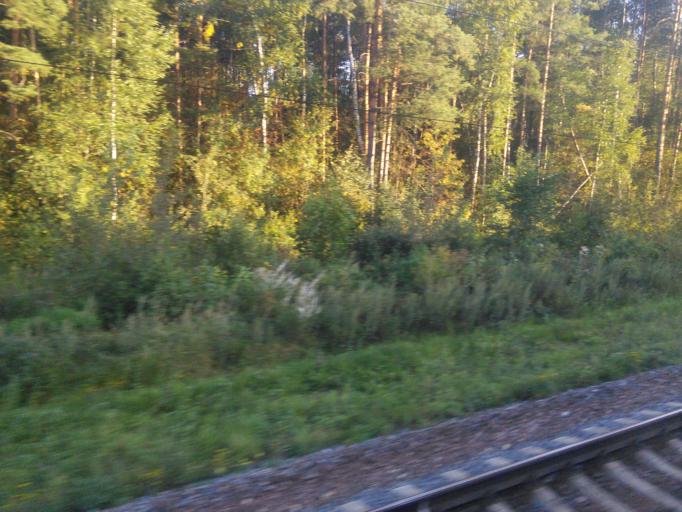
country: RU
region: Moskovskaya
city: Rakhmanovo
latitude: 55.7640
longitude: 38.6049
